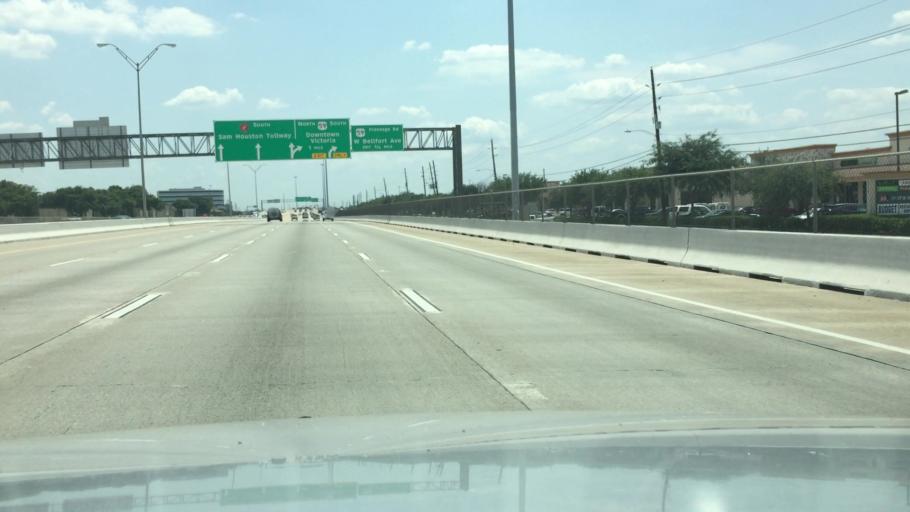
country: US
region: Texas
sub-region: Fort Bend County
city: Meadows Place
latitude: 29.6833
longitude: -95.5588
